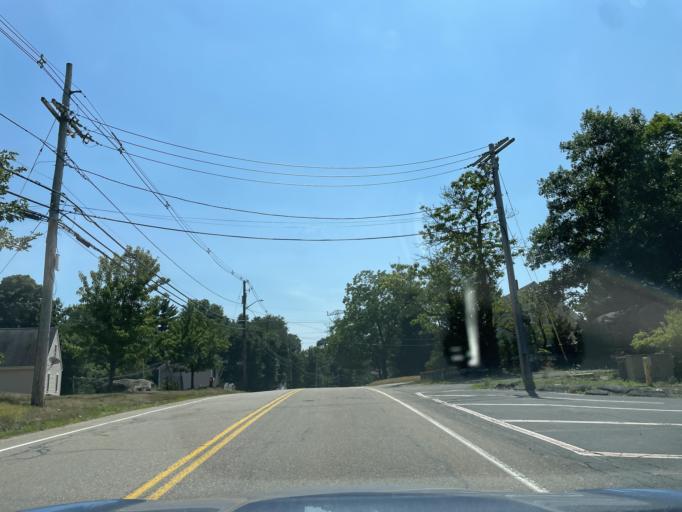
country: US
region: Massachusetts
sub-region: Norfolk County
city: Holbrook
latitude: 42.1606
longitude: -71.0245
